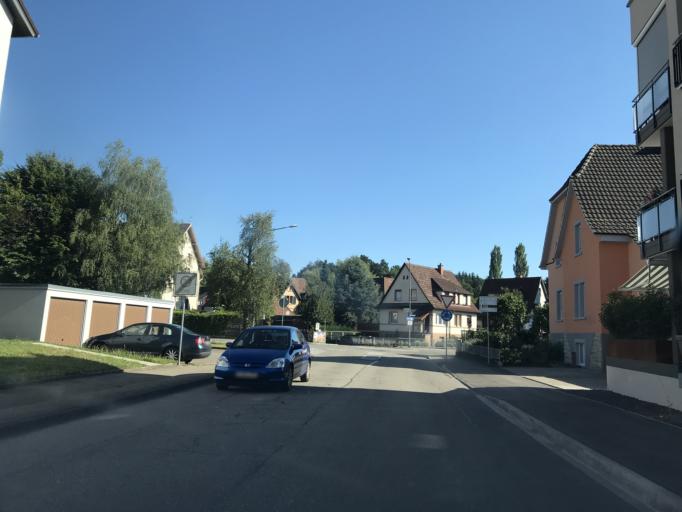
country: DE
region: Baden-Wuerttemberg
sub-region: Freiburg Region
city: Schopfheim
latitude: 47.6499
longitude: 7.8311
